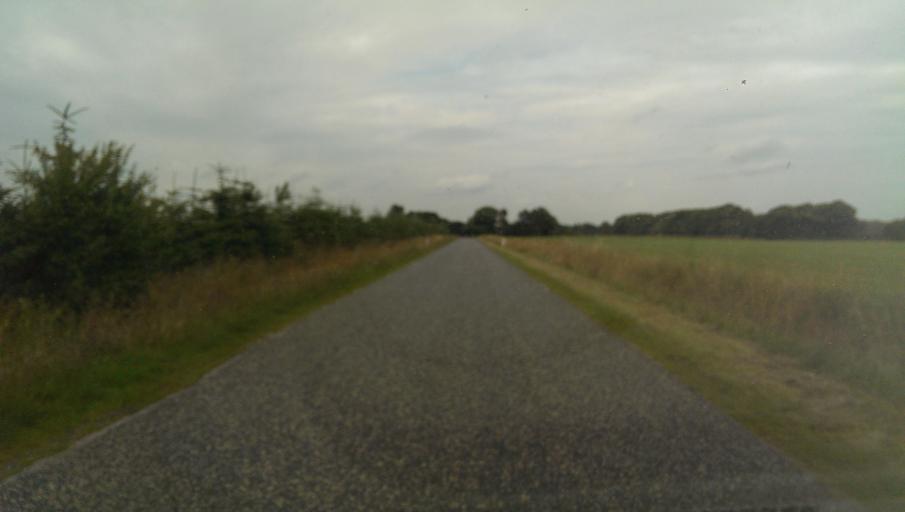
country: DK
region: South Denmark
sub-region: Esbjerg Kommune
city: Bramming
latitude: 55.4709
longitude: 8.7316
